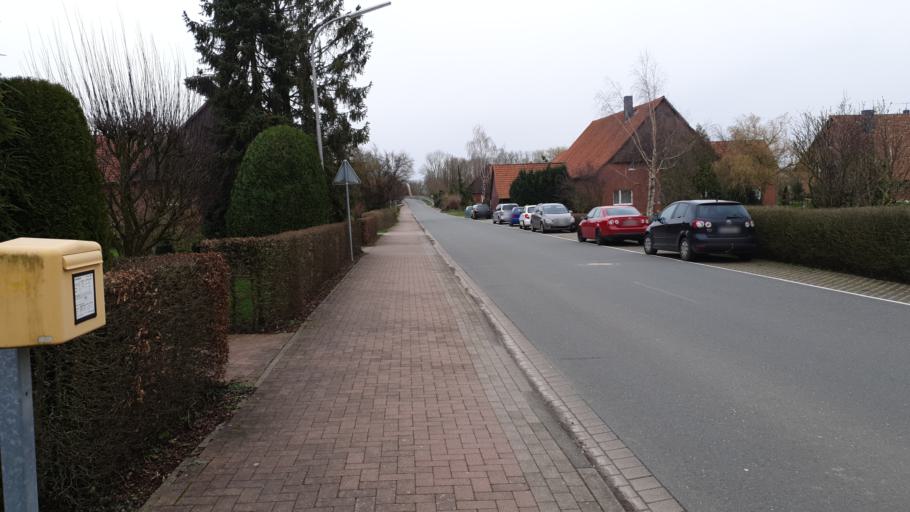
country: DE
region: Lower Saxony
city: Ludersfeld
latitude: 52.3823
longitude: 9.2278
